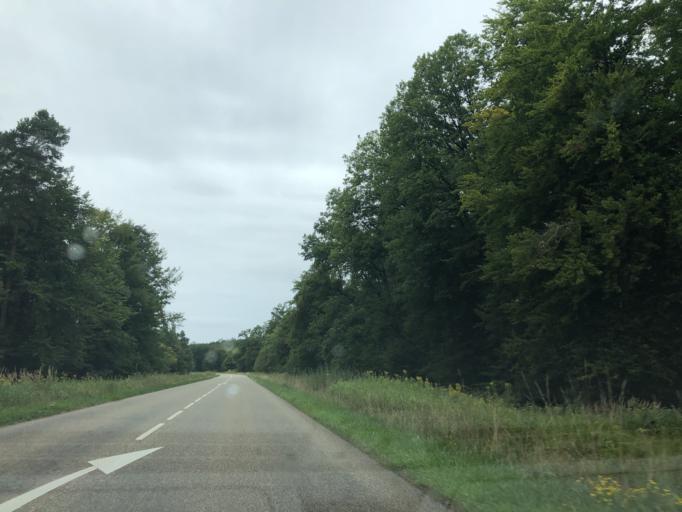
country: DE
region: Rheinland-Pfalz
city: Scheibenhardt
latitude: 48.9851
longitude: 8.1088
